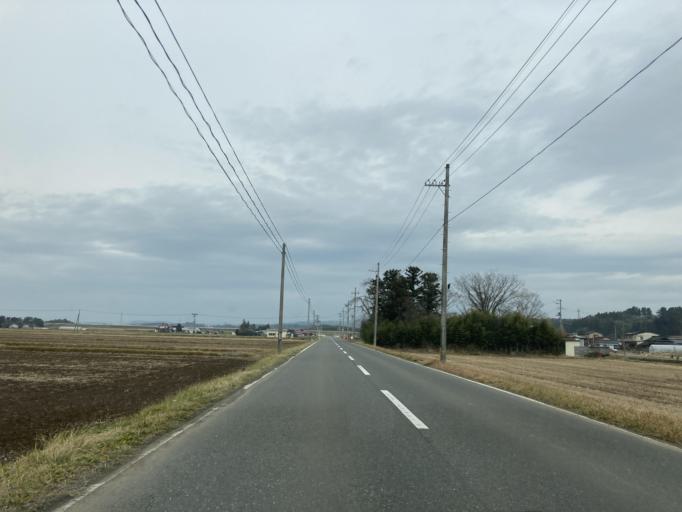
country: JP
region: Miyagi
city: Wakuya
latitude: 38.6978
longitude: 141.2720
